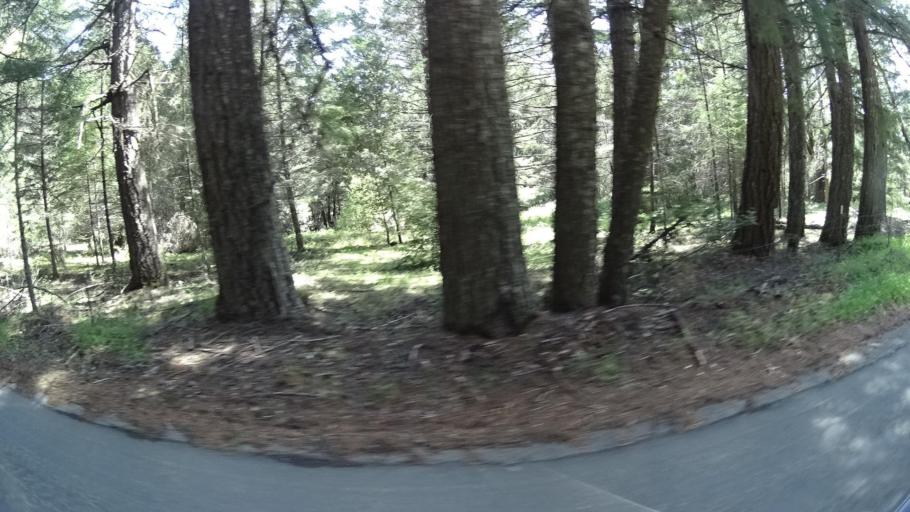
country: US
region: California
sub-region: Humboldt County
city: Redway
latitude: 40.0327
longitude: -123.6382
